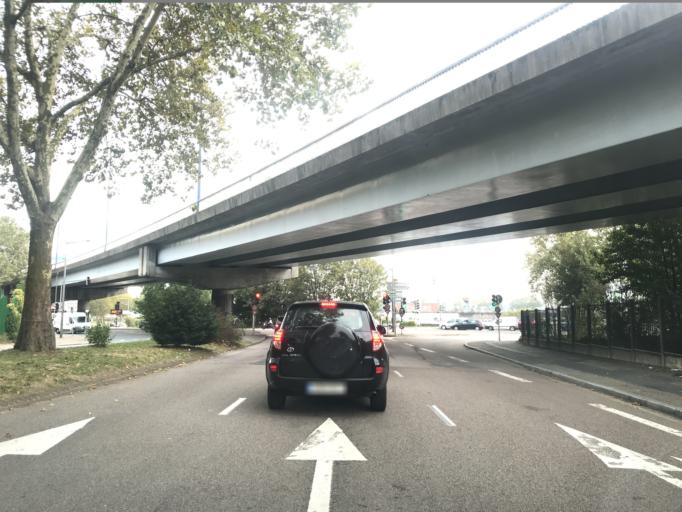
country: FR
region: Haute-Normandie
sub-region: Departement de la Seine-Maritime
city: Deville-les-Rouen
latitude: 49.4514
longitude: 1.0570
